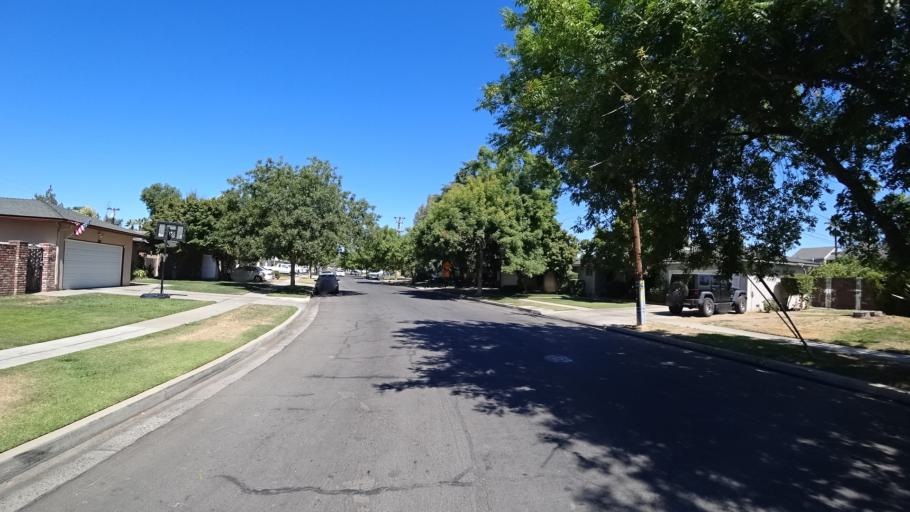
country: US
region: California
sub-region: Fresno County
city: Fresno
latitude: 36.7897
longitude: -119.8187
